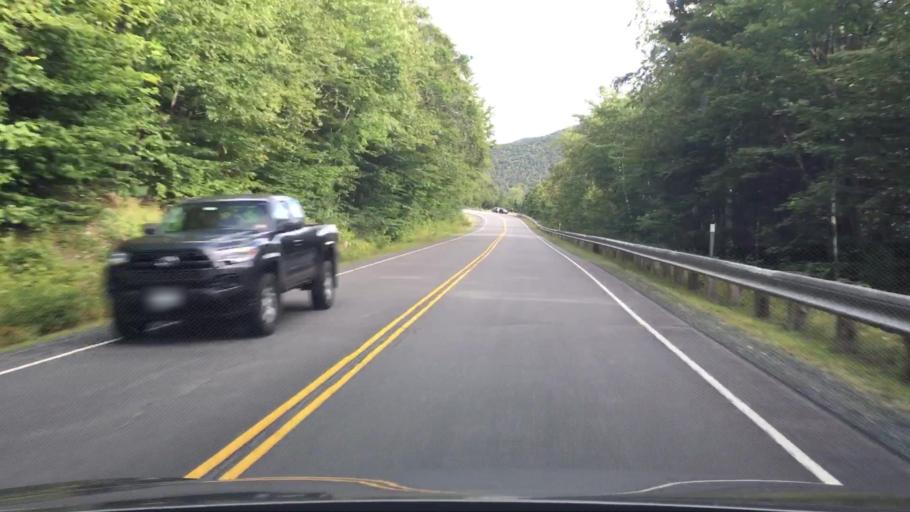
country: US
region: New Hampshire
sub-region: Grafton County
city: Woodstock
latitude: 44.0362
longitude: -71.5188
